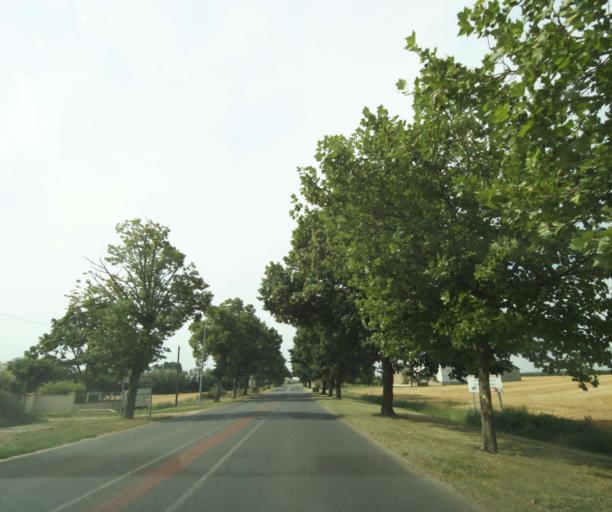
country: FR
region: Centre
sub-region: Departement d'Indre-et-Loire
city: Neuille-Pont-Pierre
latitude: 47.5515
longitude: 0.5497
